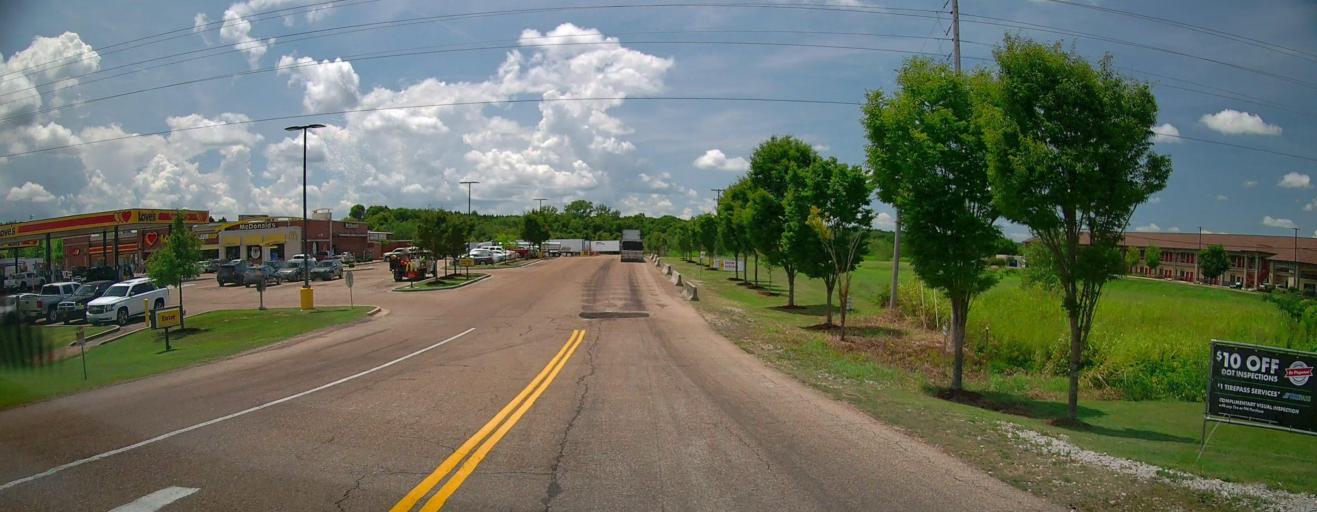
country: US
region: Mississippi
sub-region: Lee County
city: Tupelo
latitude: 34.3168
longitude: -88.7924
